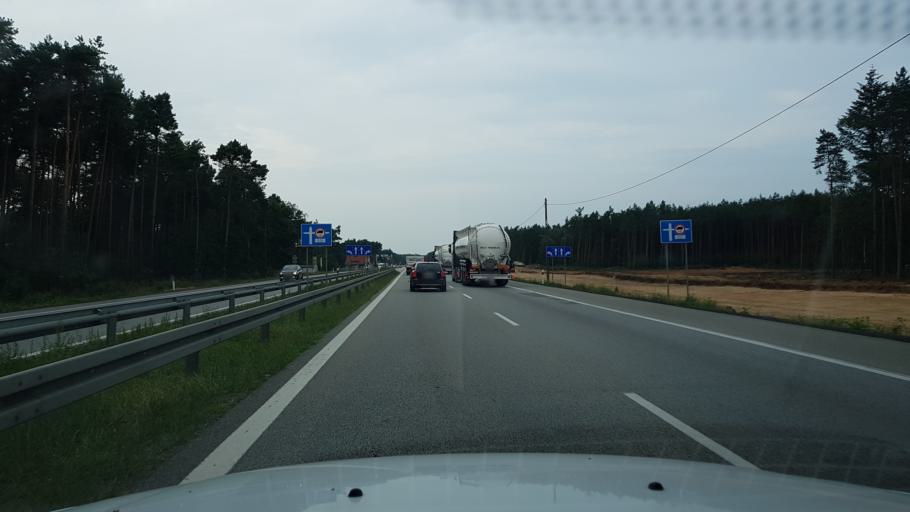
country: PL
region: West Pomeranian Voivodeship
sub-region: Powiat goleniowski
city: Goleniow
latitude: 53.4582
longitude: 14.7881
